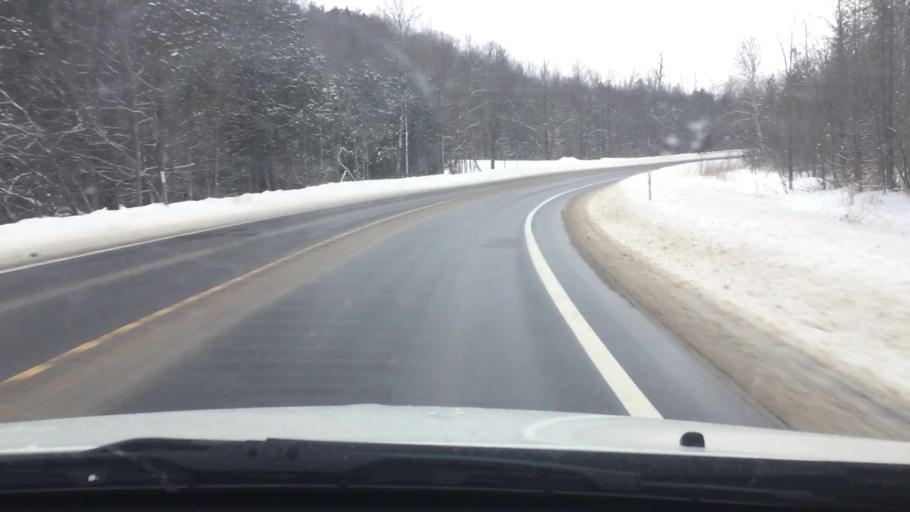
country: US
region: Michigan
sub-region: Charlevoix County
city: East Jordan
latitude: 45.1290
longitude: -85.0795
